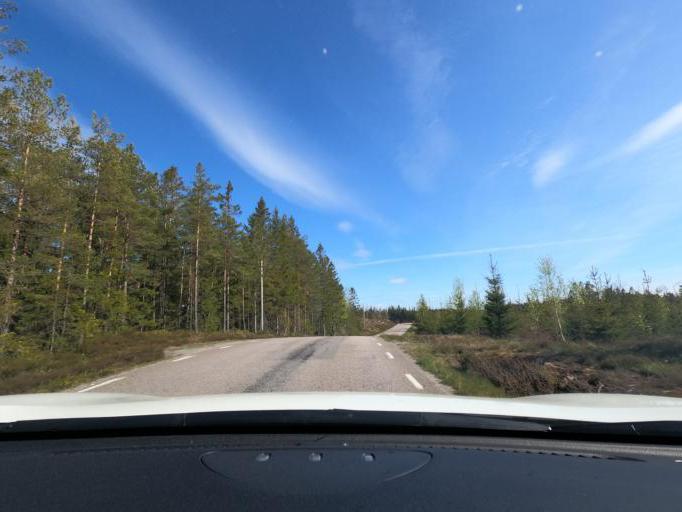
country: SE
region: Vaestra Goetaland
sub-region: Harryda Kommun
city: Hindas
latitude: 57.6609
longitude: 12.3555
